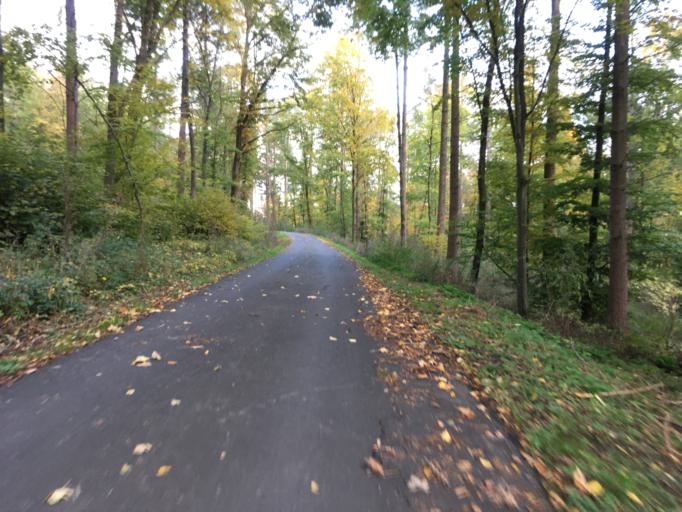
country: DE
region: Baden-Wuerttemberg
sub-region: Karlsruhe Region
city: Seckach
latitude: 49.4729
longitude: 9.3697
